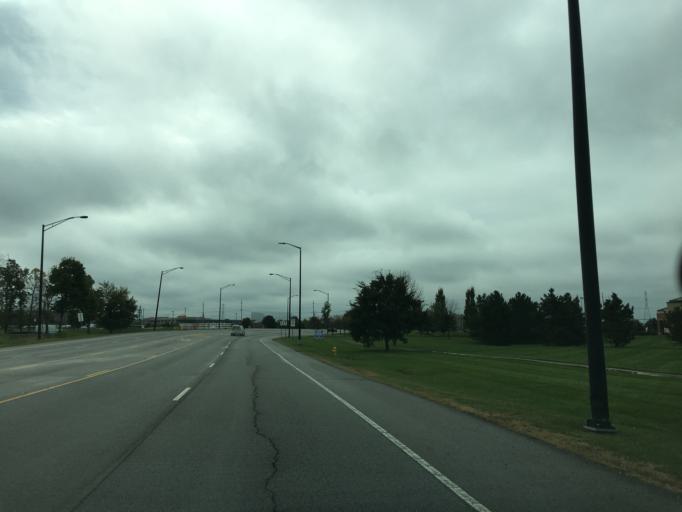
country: US
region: Ohio
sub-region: Butler County
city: Beckett Ridge
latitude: 39.3326
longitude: -84.4360
